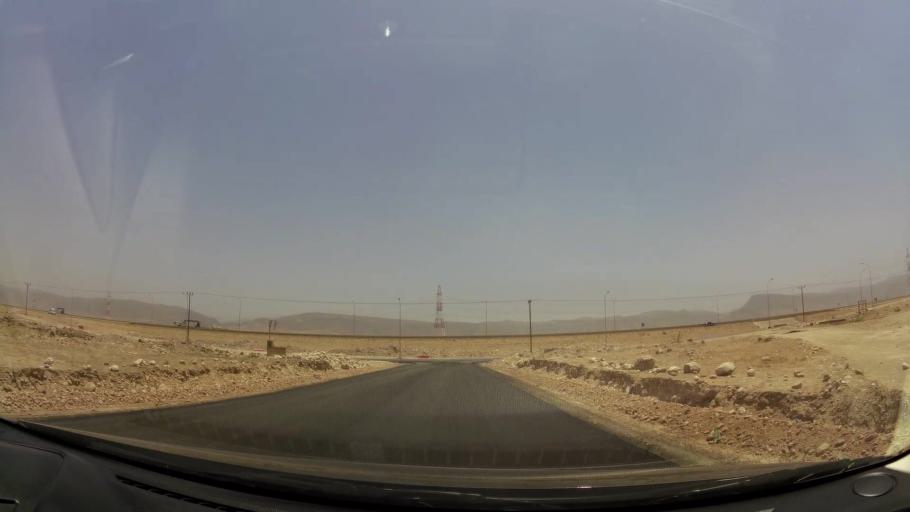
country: OM
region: Zufar
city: Salalah
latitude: 17.1009
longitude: 54.1662
